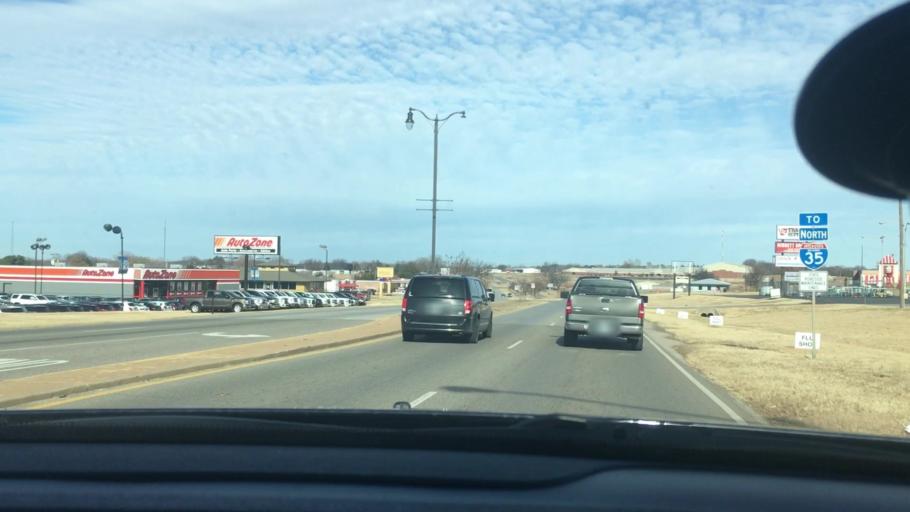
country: US
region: Oklahoma
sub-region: McClain County
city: Purcell
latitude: 35.0299
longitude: -97.3661
